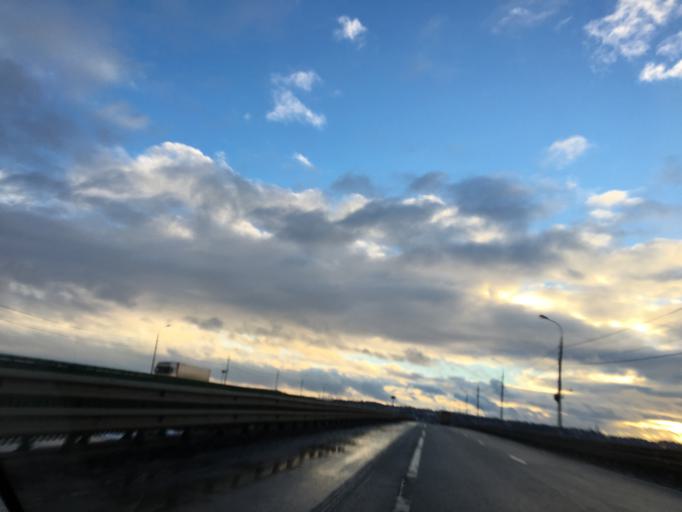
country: RU
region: Moskovskaya
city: Danki
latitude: 54.8714
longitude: 37.5046
